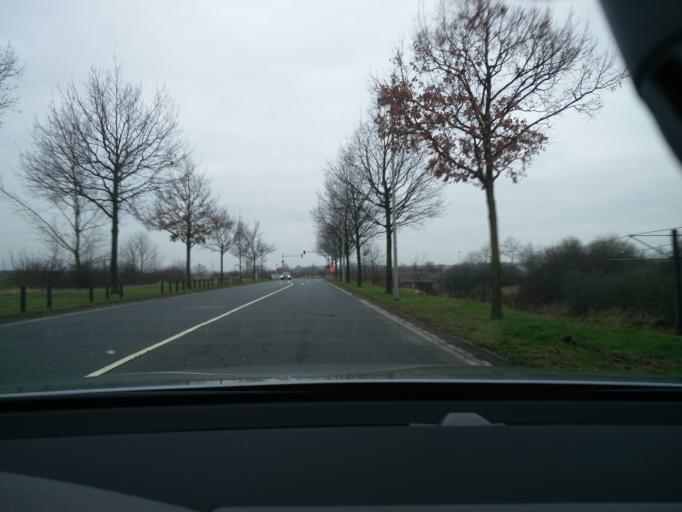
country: DE
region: Lower Saxony
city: Laatzen
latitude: 52.3311
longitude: 9.8278
